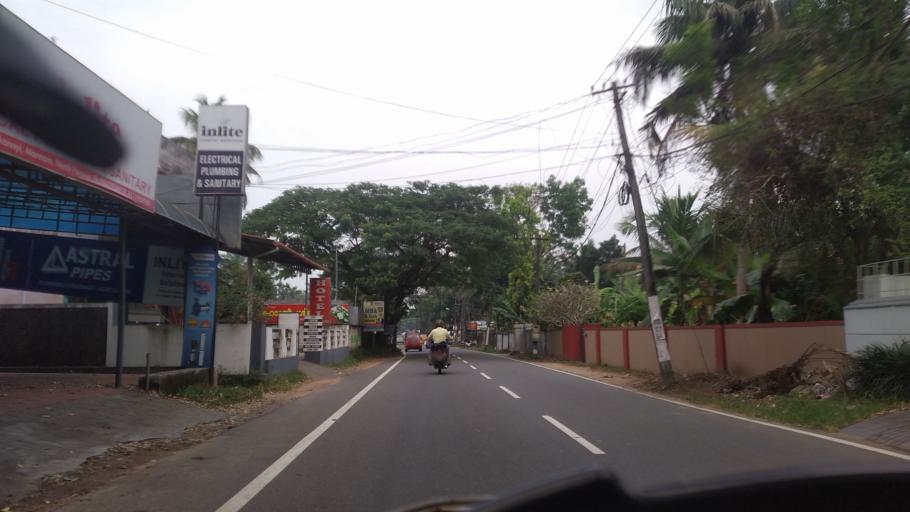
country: IN
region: Kerala
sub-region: Ernakulam
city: Elur
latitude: 10.1494
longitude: 76.2538
